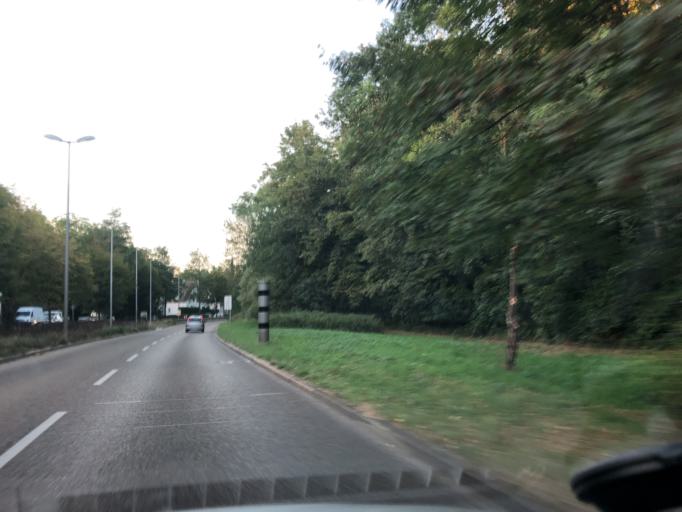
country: DE
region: Baden-Wuerttemberg
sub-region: Regierungsbezirk Stuttgart
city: Ludwigsburg
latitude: 48.9050
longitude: 9.2136
